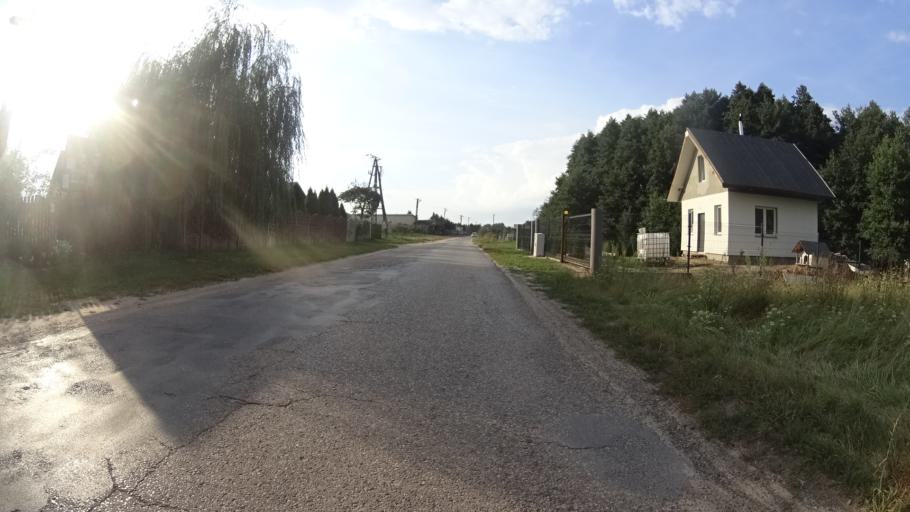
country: PL
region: Masovian Voivodeship
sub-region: Powiat grojecki
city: Mogielnica
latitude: 51.6761
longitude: 20.7367
